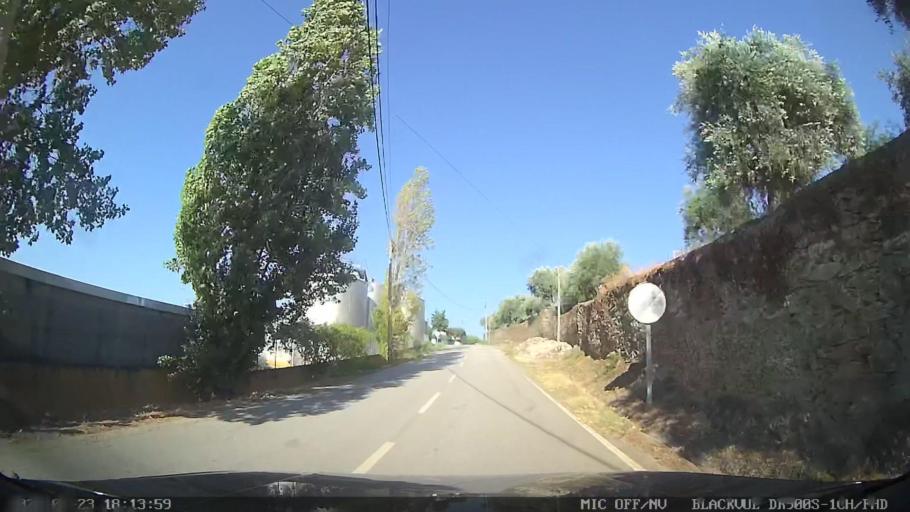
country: PT
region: Viseu
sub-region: Sao Joao da Pesqueira
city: Sao Joao da Pesqueira
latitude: 41.1880
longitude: -7.4254
